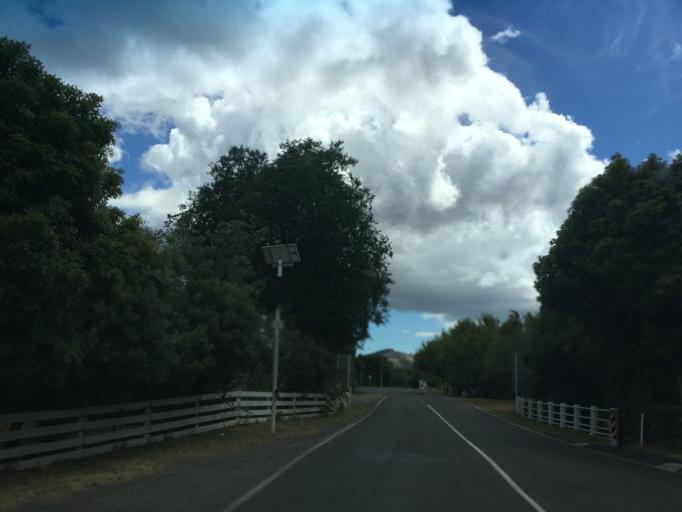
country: NZ
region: Hawke's Bay
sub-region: Hastings District
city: Hastings
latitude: -39.7190
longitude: 176.9289
